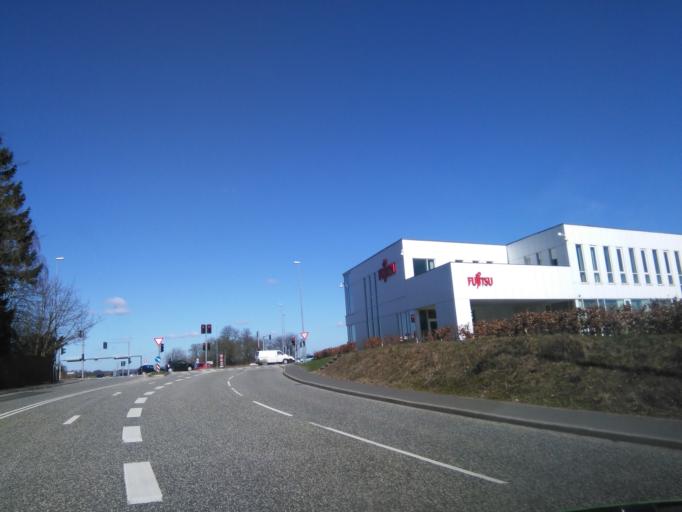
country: DK
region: Central Jutland
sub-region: Arhus Kommune
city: Tranbjerg
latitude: 56.1085
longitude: 10.1192
